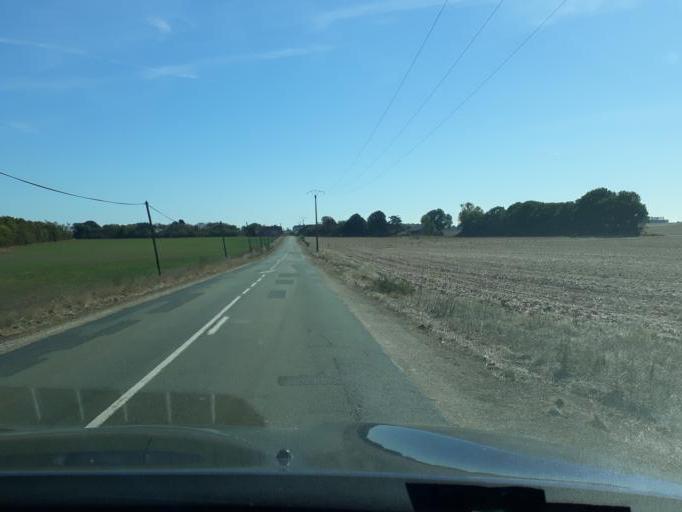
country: FR
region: Centre
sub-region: Departement du Loir-et-Cher
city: Ouzouer-le-Marche
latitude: 47.9314
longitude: 1.5172
